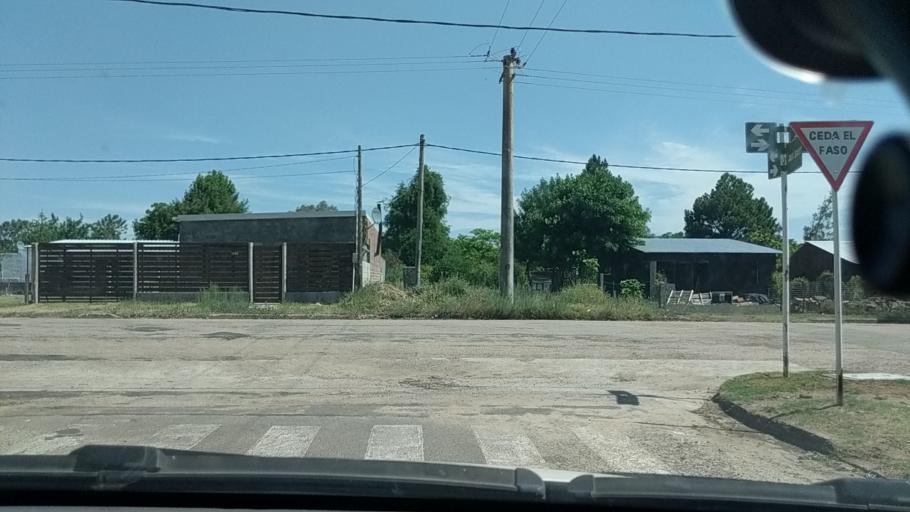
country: UY
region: Tacuarembo
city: Paso de los Toros
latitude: -32.8100
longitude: -56.5305
